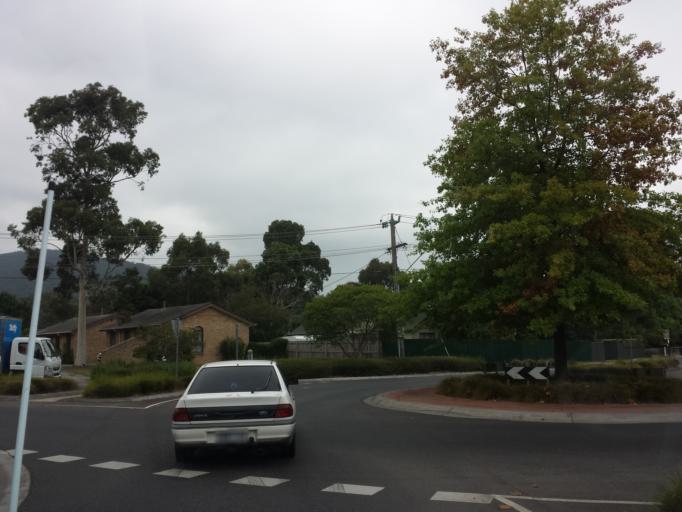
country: AU
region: Victoria
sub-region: Knox
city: The Basin
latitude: -37.8530
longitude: 145.2984
